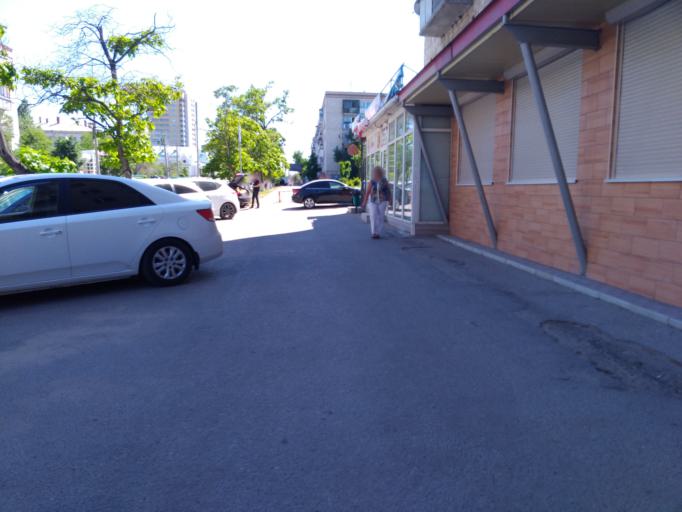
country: RU
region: Volgograd
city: Volgograd
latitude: 48.7224
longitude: 44.5306
